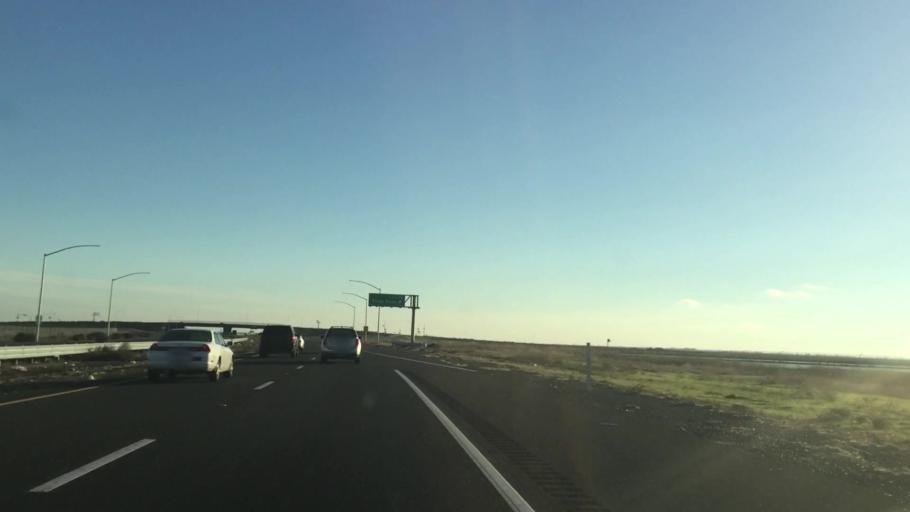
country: US
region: California
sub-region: Sacramento County
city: Elverta
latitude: 38.7575
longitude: -121.5435
